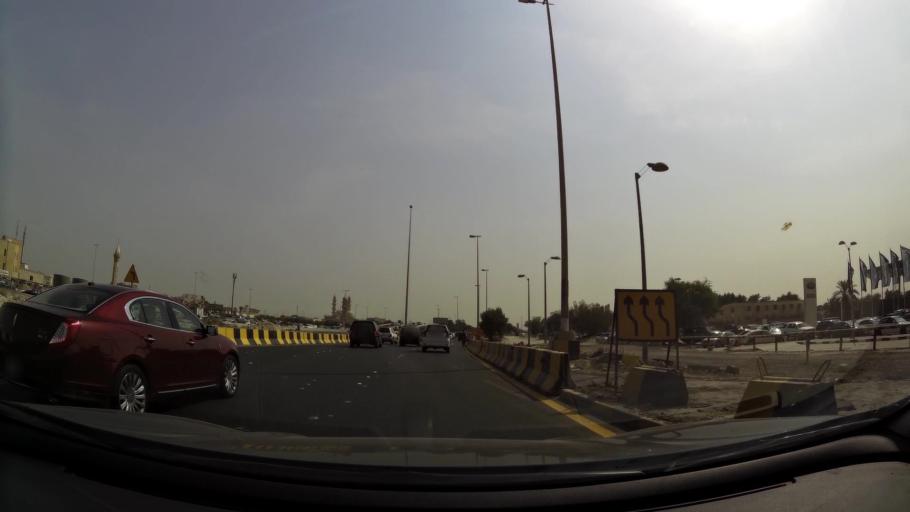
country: KW
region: Al Asimah
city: Ash Shamiyah
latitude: 29.3362
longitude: 47.9493
